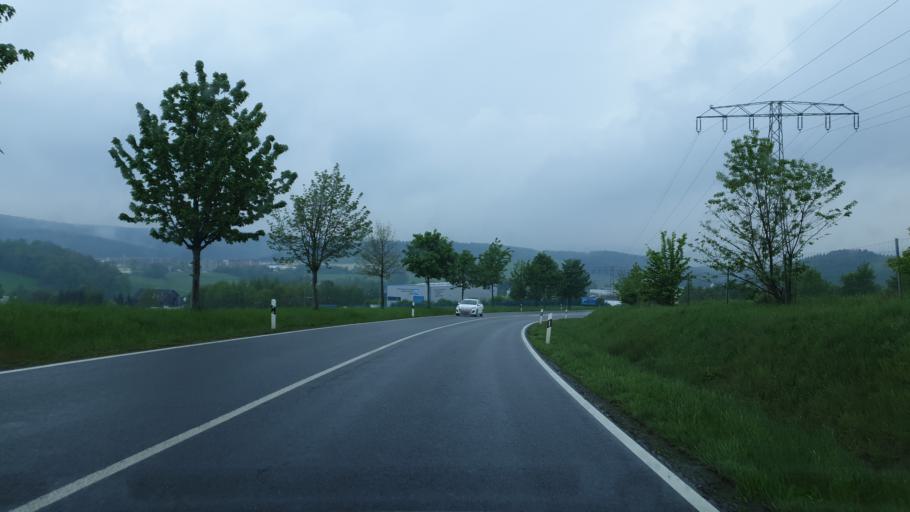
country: DE
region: Saxony
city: Lossnitz
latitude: 50.6214
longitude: 12.7052
